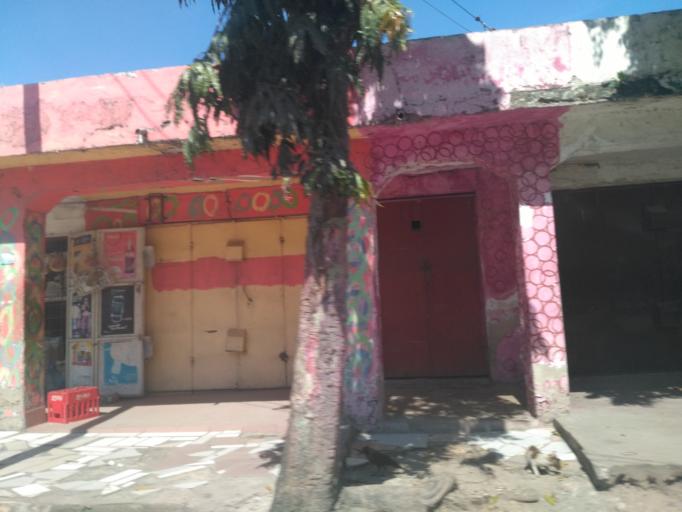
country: TZ
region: Dar es Salaam
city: Magomeni
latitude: -6.7890
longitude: 39.2648
